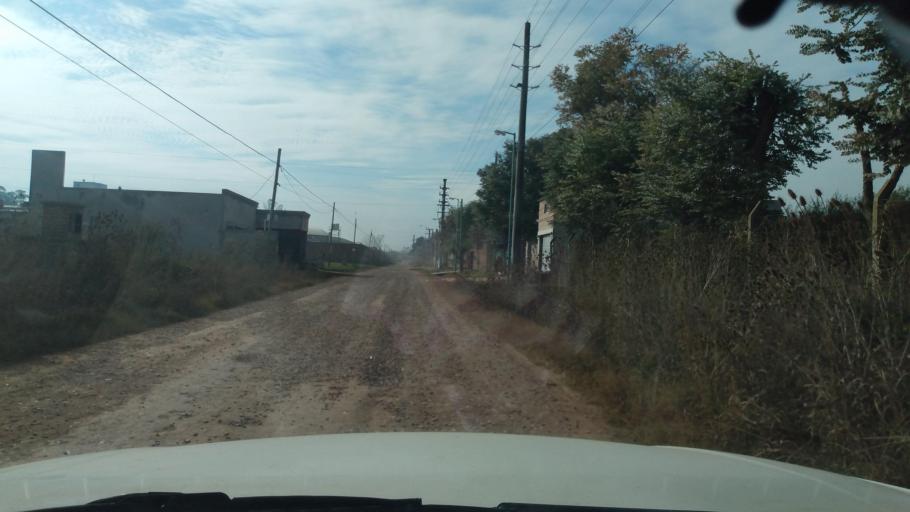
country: AR
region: Buenos Aires
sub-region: Partido de Lujan
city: Lujan
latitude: -34.5862
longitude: -59.1218
